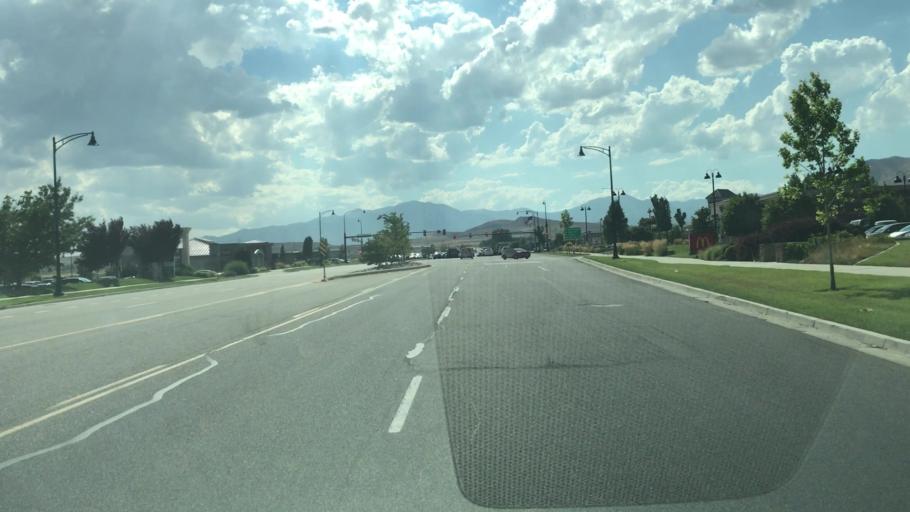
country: US
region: Utah
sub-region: Utah County
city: Saratoga Springs
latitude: 40.3875
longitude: -111.9137
